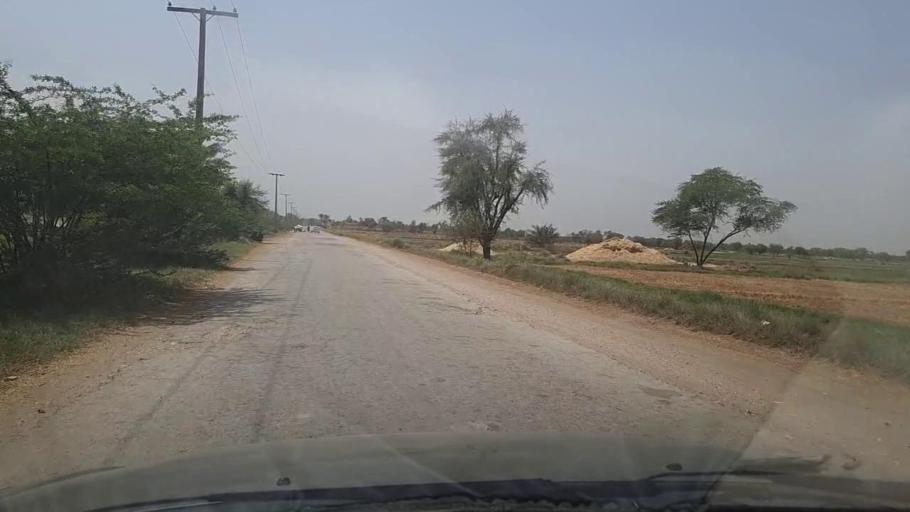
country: PK
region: Sindh
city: Bhiria
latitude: 26.8961
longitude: 68.2334
